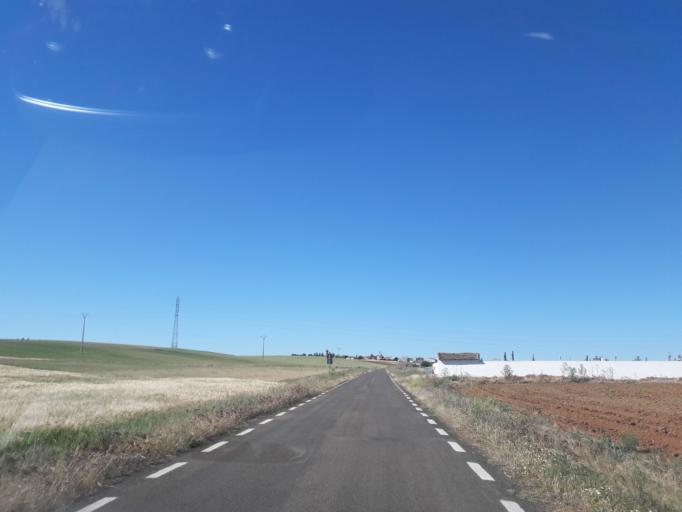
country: ES
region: Castille and Leon
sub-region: Provincia de Salamanca
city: Parada de Arriba
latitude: 40.9949
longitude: -5.7886
